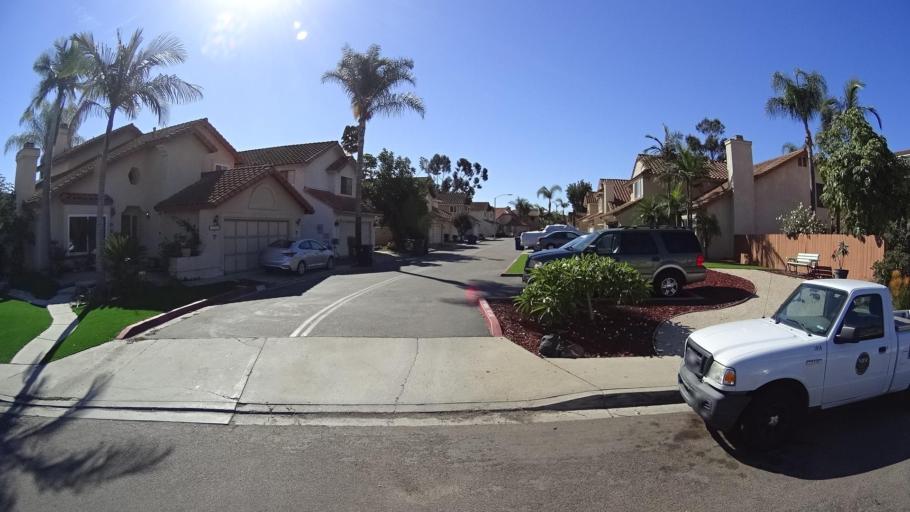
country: US
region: California
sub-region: San Diego County
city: La Presa
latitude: 32.7172
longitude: -116.9790
